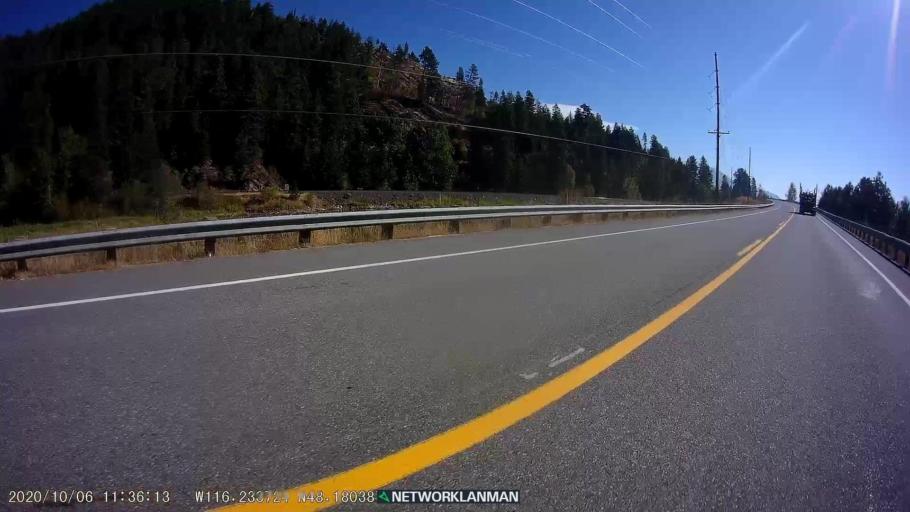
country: US
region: Idaho
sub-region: Bonner County
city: Ponderay
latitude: 48.1803
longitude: -116.2336
